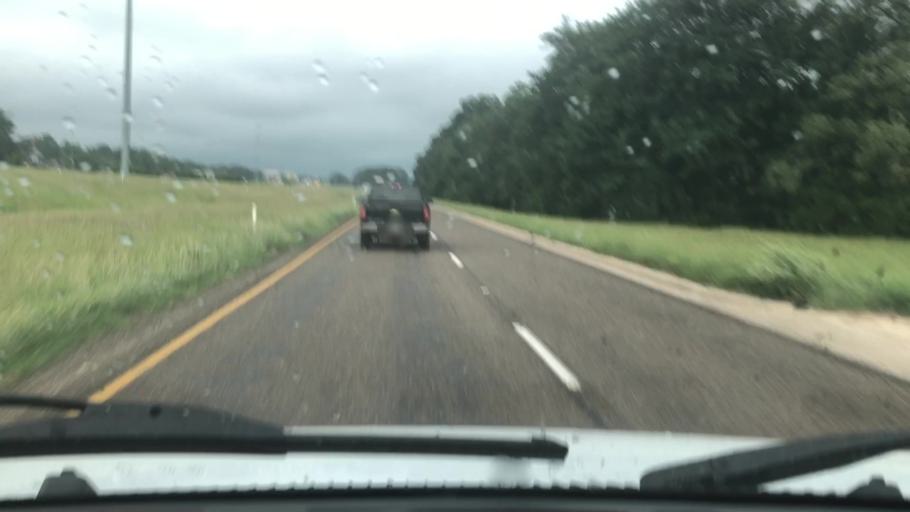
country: US
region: Texas
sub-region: Bowie County
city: Wake Village
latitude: 33.4392
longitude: -94.0974
